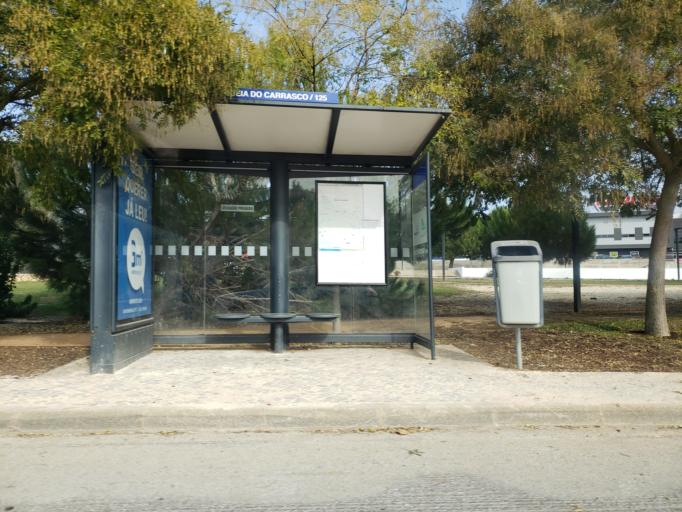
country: PT
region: Faro
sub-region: Portimao
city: Portimao
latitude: 37.1520
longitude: -8.5553
